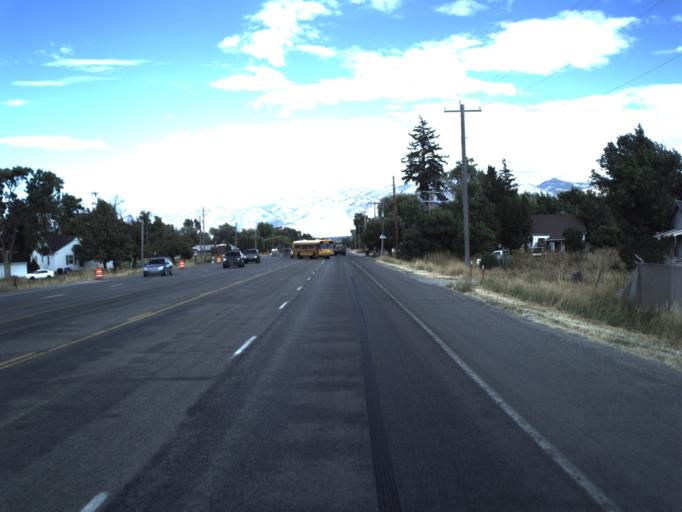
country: US
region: Utah
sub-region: Cache County
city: Nibley
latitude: 41.6760
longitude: -111.8824
